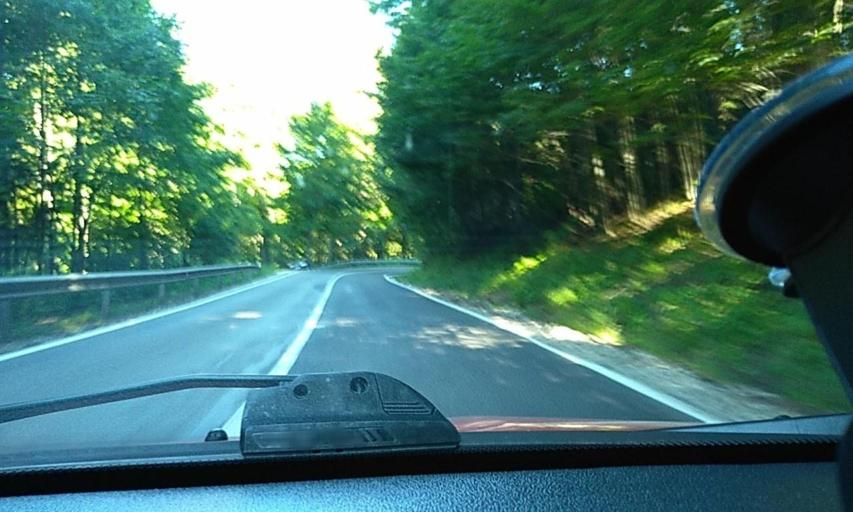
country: RO
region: Brasov
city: Crivina
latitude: 45.4921
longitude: 25.8701
